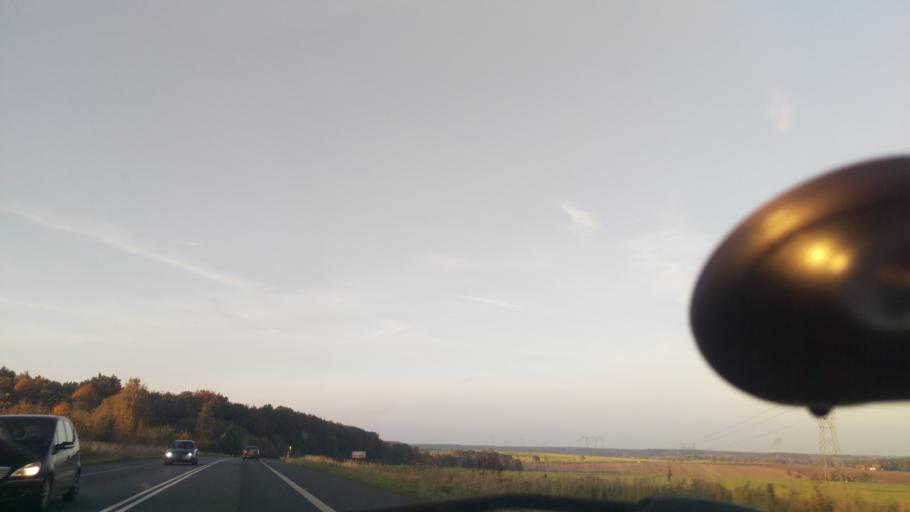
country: PL
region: West Pomeranian Voivodeship
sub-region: Powiat gryfinski
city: Stare Czarnowo
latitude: 53.2935
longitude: 14.7888
